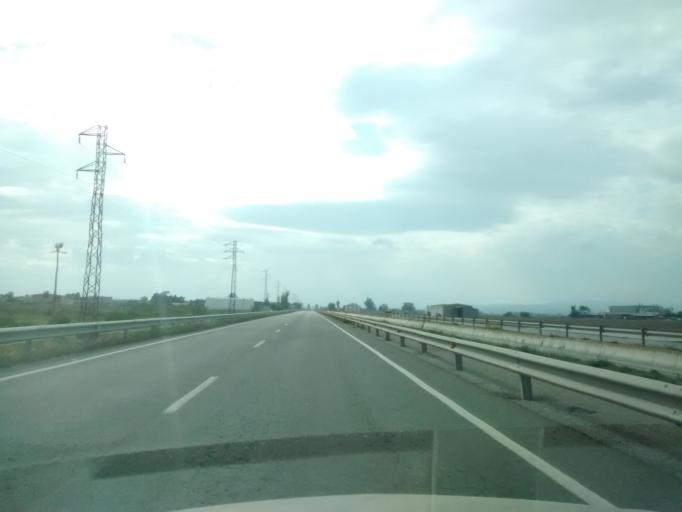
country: ES
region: Catalonia
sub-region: Provincia de Tarragona
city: Deltebre
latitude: 40.7251
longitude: 0.7178
